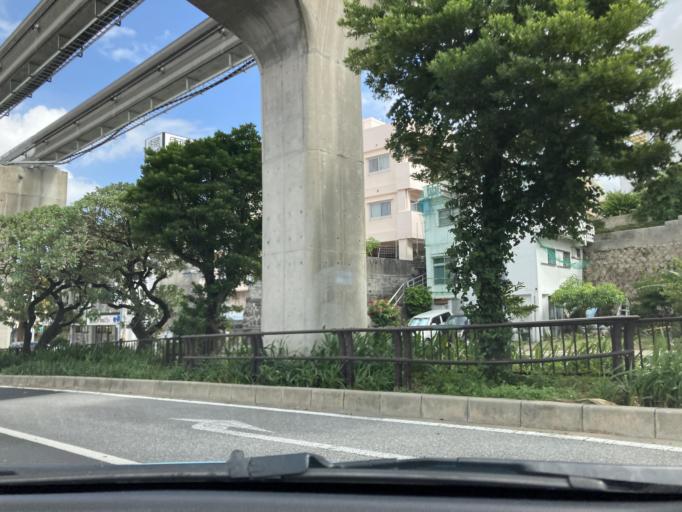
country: JP
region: Okinawa
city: Naha-shi
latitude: 26.1998
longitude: 127.6727
